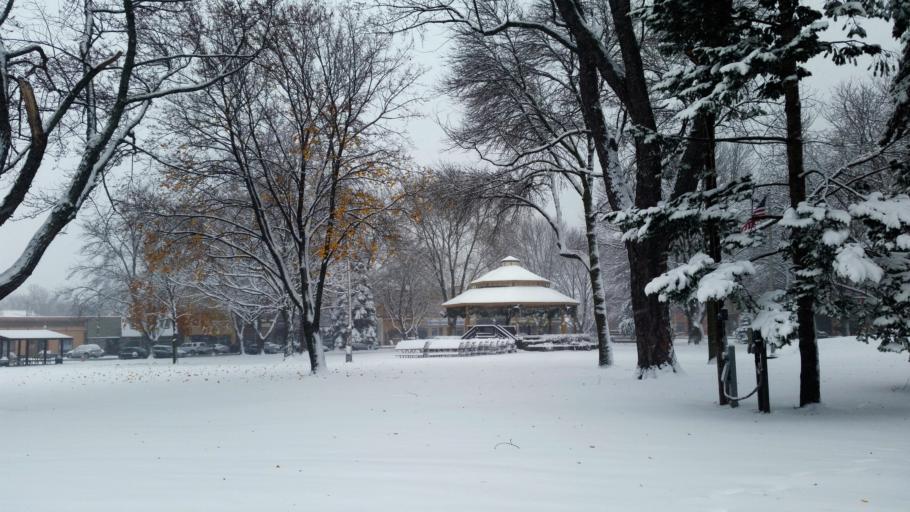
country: US
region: Wisconsin
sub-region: Jefferson County
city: Lake Mills
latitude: 43.0807
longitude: -88.9111
